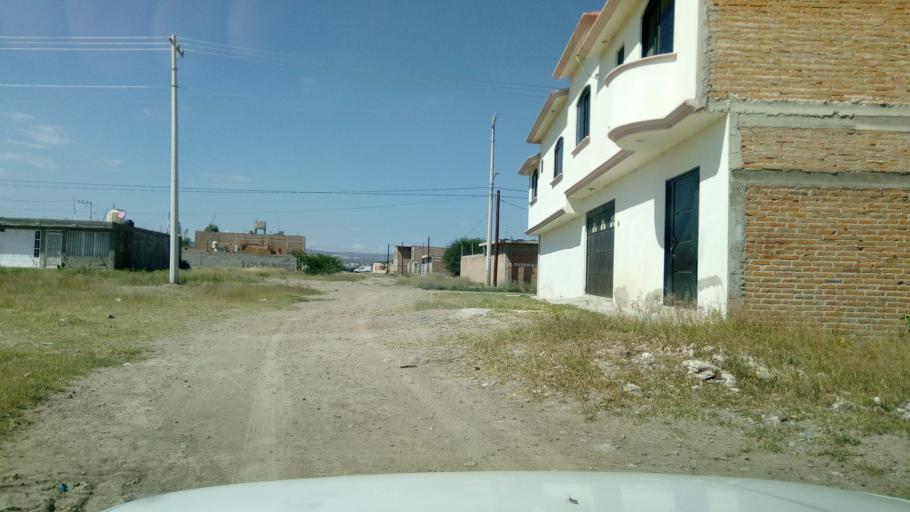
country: MX
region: Durango
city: Victoria de Durango
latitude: 23.9843
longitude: -104.6797
